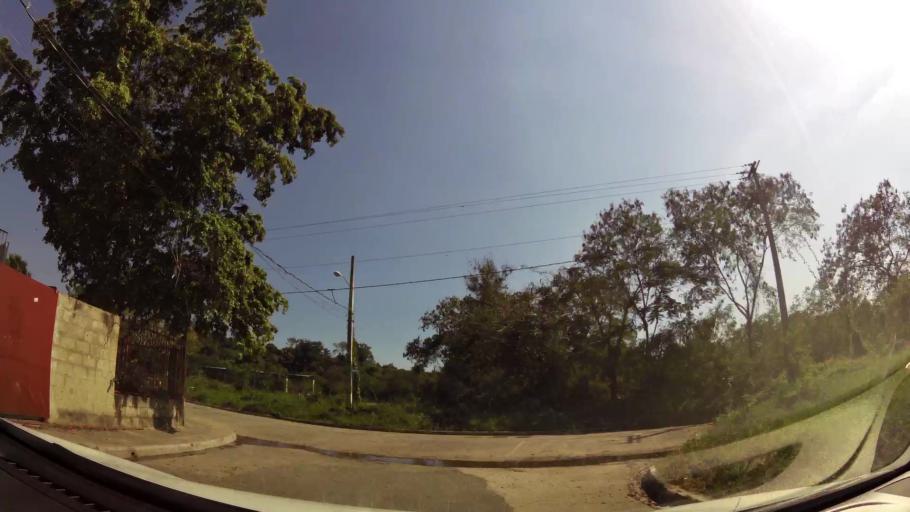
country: DO
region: San Cristobal
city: El Carril
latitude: 18.4705
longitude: -70.0087
